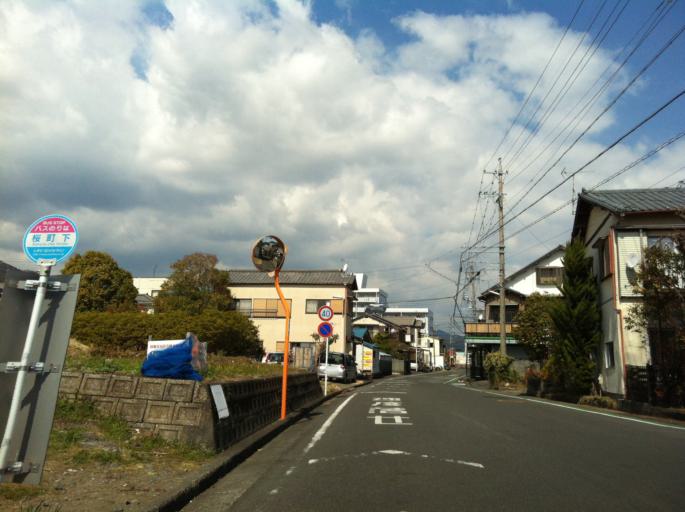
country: JP
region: Shizuoka
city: Shizuoka-shi
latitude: 34.9931
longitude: 138.3611
